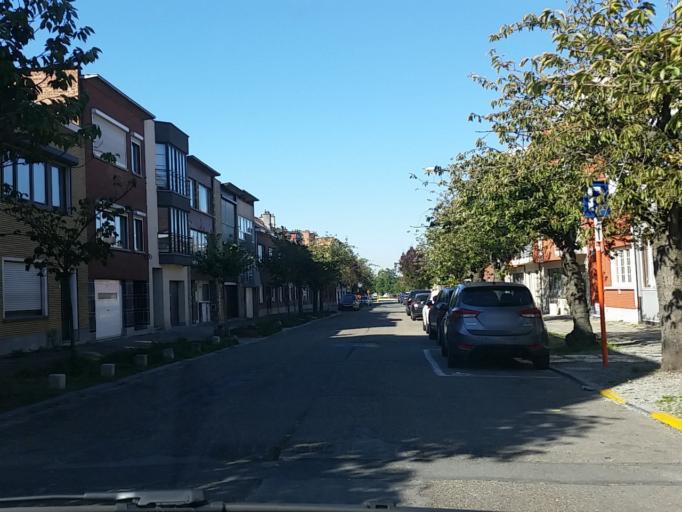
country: BE
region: Flanders
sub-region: Provincie Vlaams-Brabant
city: Vilvoorde
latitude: 50.9351
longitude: 4.4313
